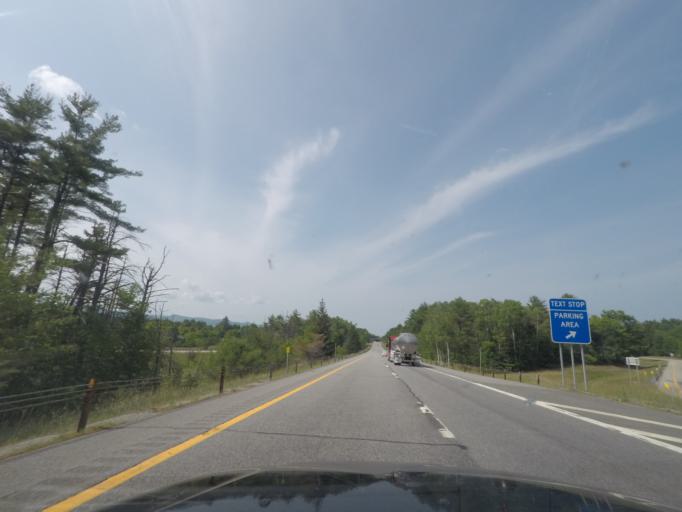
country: US
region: New York
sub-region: Essex County
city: Elizabethtown
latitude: 44.1592
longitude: -73.5831
